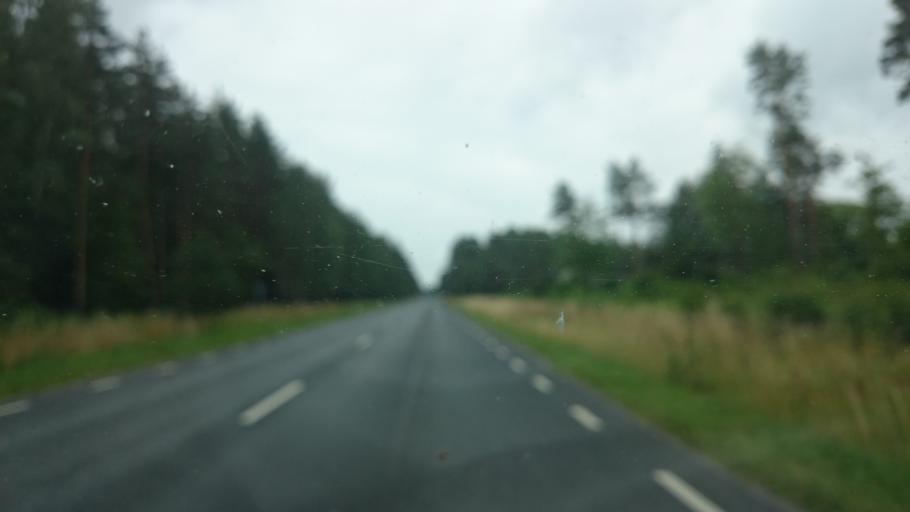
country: EE
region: Saare
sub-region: Orissaare vald
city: Orissaare
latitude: 58.5981
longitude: 23.3225
